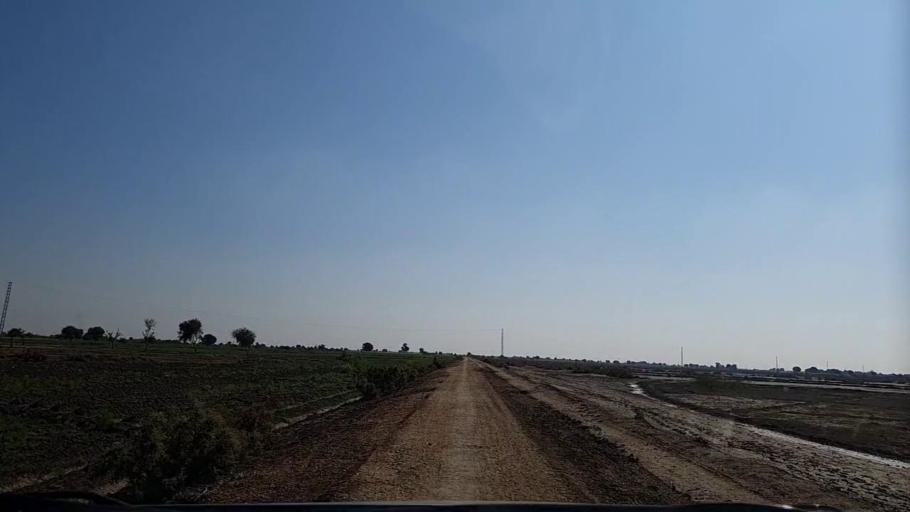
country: PK
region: Sindh
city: Pithoro
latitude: 25.7012
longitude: 69.3401
